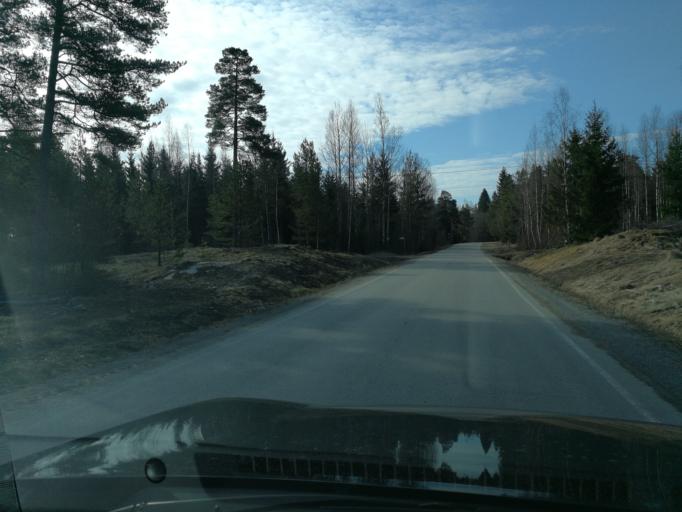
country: FI
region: Uusimaa
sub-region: Raaseporin
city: Inga
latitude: 60.0610
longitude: 24.0881
